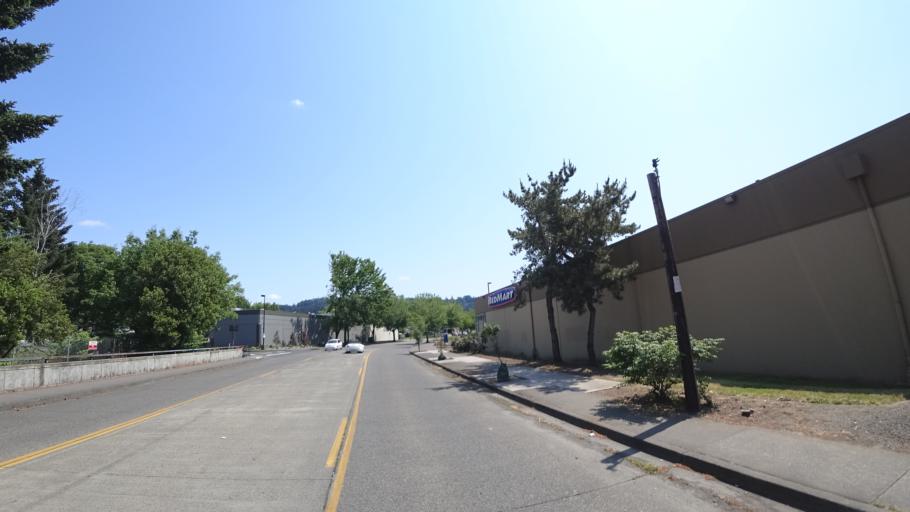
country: US
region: Oregon
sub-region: Clackamas County
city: Oatfield
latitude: 45.4410
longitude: -122.5812
